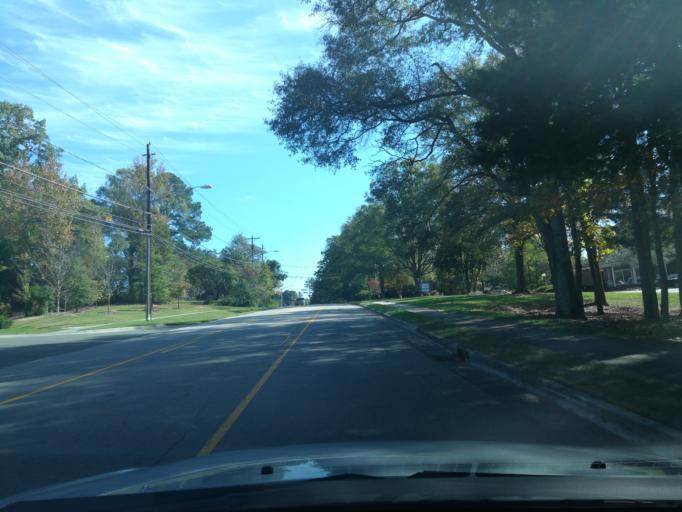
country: US
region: North Carolina
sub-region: Durham County
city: Durham
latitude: 35.9749
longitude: -78.9631
